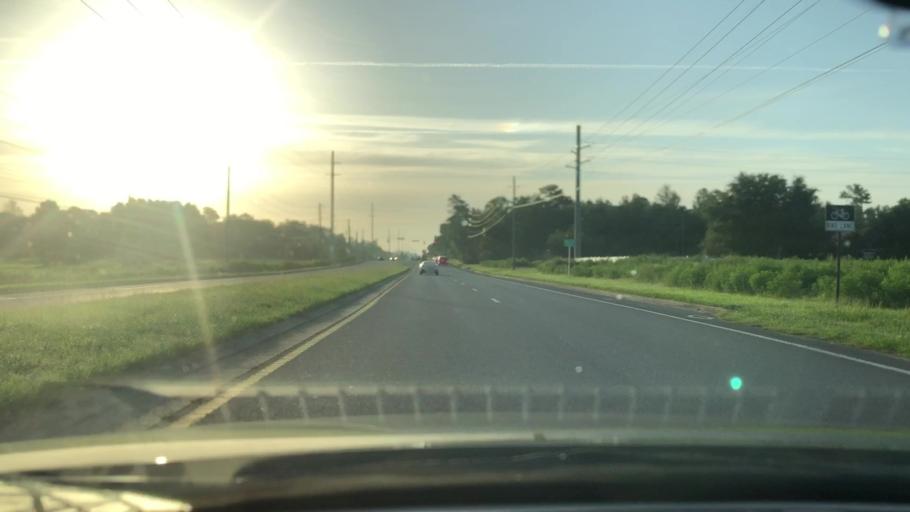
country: US
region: Florida
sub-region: Marion County
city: Belleview
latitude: 29.0260
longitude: -82.1998
